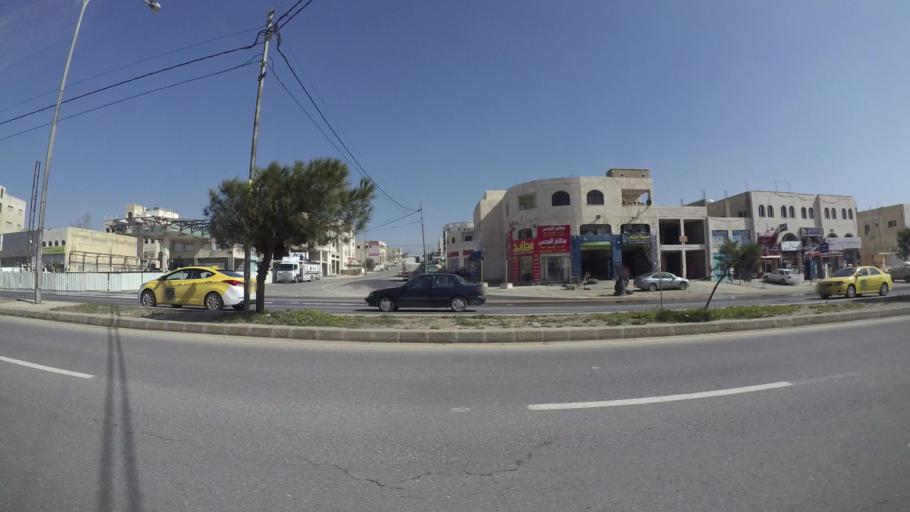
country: JO
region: Amman
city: Al Bunayyat ash Shamaliyah
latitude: 31.8983
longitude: 35.8988
